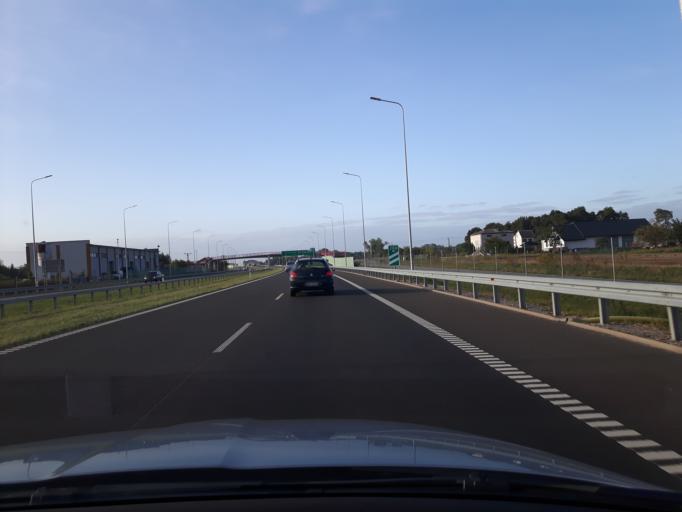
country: PL
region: Masovian Voivodeship
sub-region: Powiat radomski
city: Wolanow
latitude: 51.3957
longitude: 21.0225
